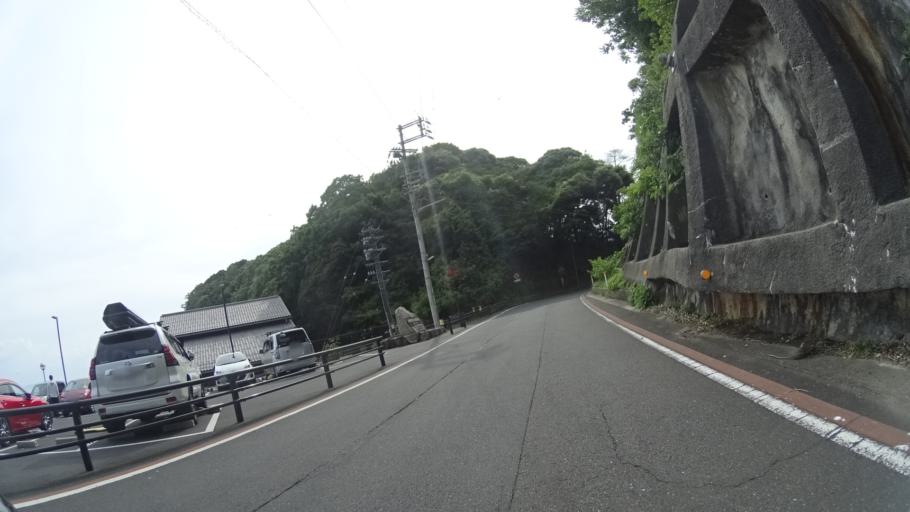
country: JP
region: Kyoto
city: Miyazu
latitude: 35.6684
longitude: 135.2808
